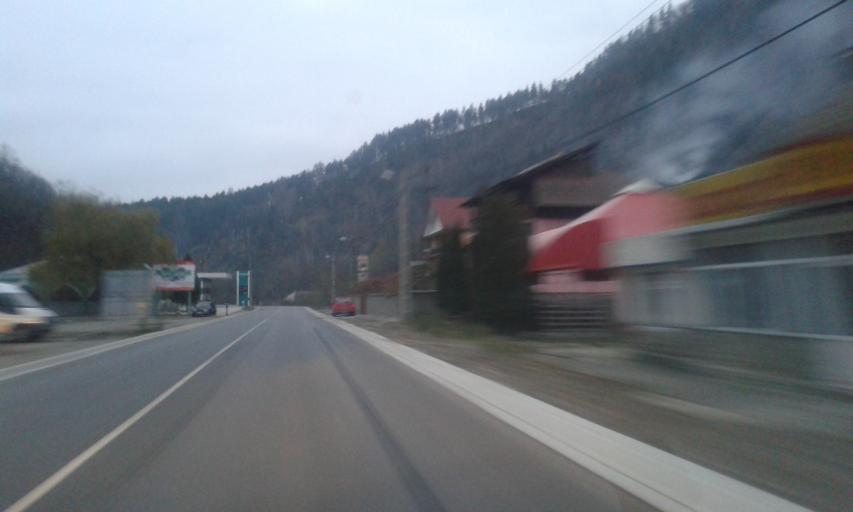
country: RO
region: Gorj
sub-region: Comuna Bumbesti-Jiu
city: Bumbesti-Jiu
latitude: 45.1954
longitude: 23.3833
